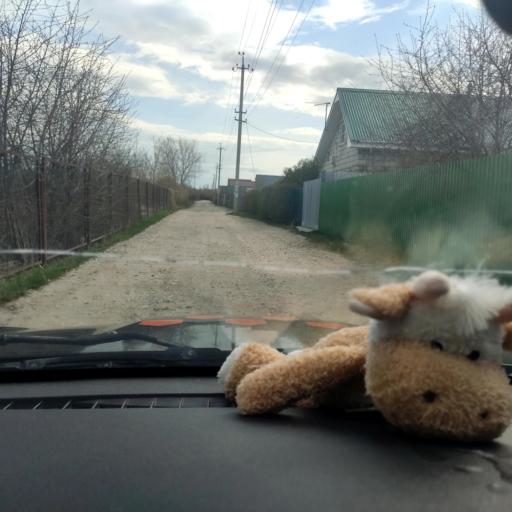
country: RU
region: Samara
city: Podstepki
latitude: 53.5917
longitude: 49.2244
